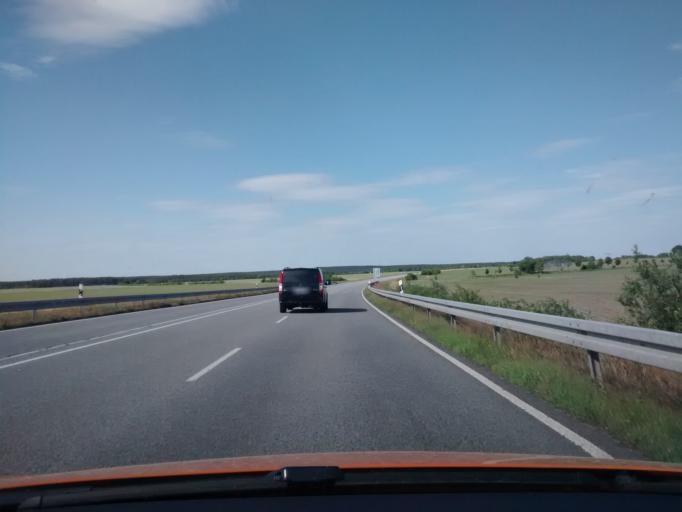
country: DE
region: Brandenburg
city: Luckenwalde
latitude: 52.1064
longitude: 13.1200
